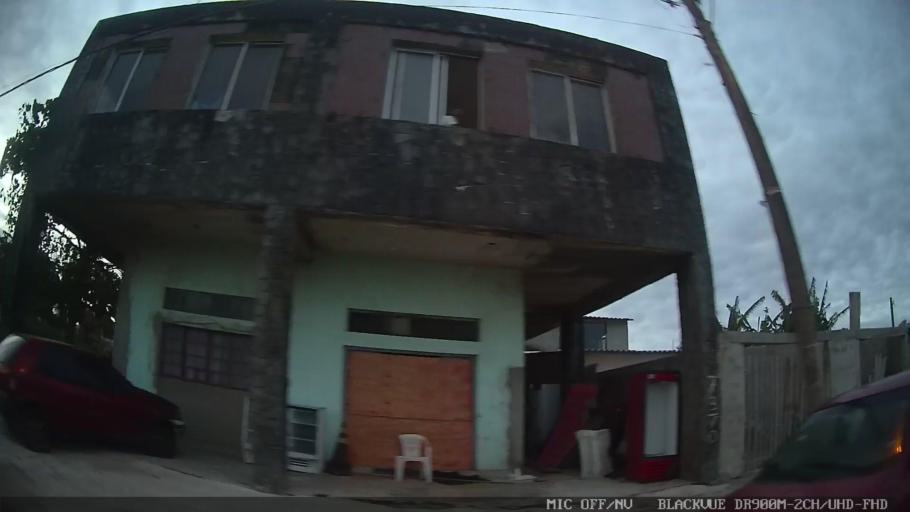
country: BR
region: Sao Paulo
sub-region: Itanhaem
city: Itanhaem
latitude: -24.2428
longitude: -46.8849
